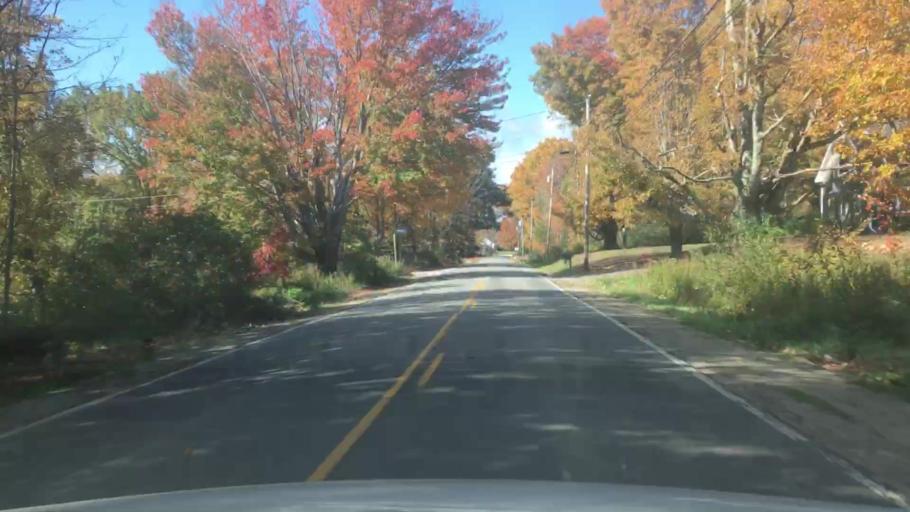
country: US
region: Maine
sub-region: Knox County
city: Warren
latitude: 44.1083
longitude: -69.2259
